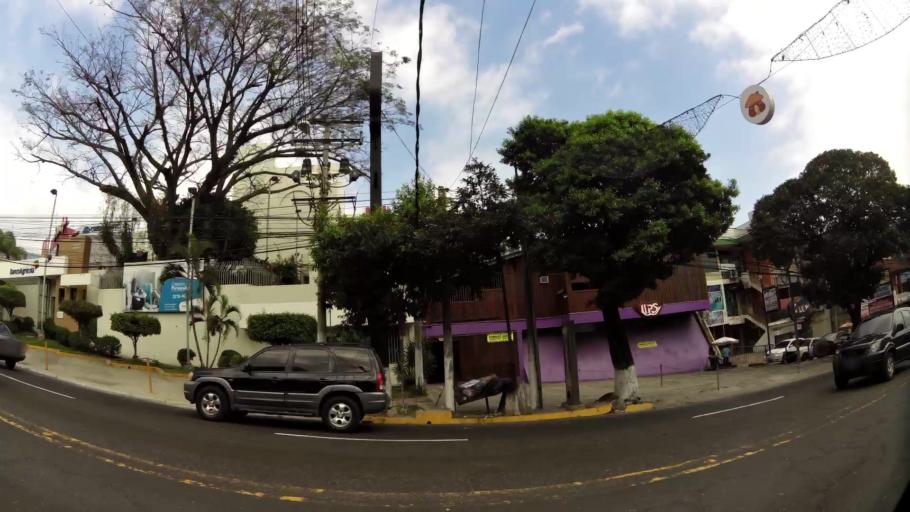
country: SV
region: La Libertad
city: Antiguo Cuscatlan
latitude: 13.7035
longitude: -89.2480
